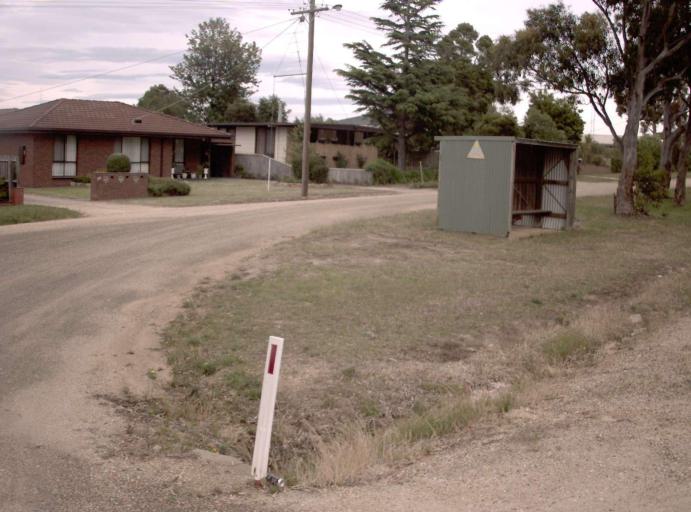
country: AU
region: Victoria
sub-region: East Gippsland
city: Bairnsdale
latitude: -37.8033
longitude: 147.6156
